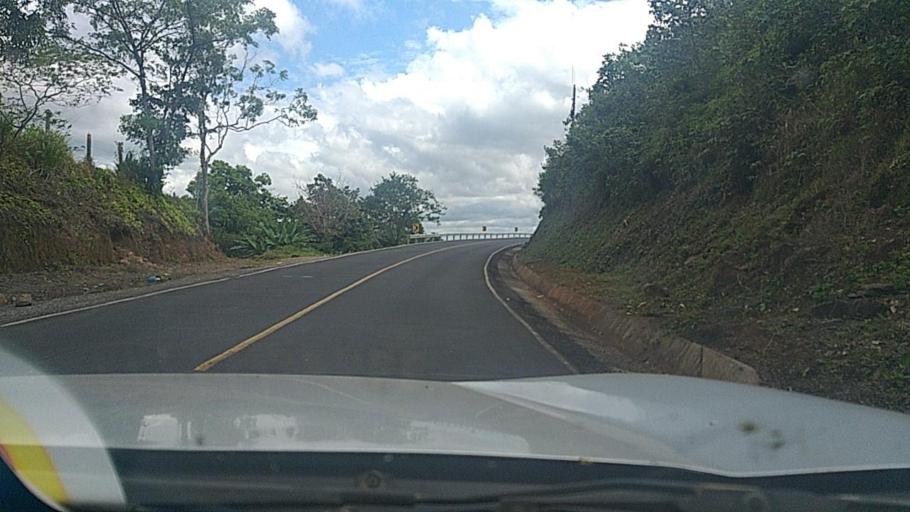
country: NI
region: Atlantico Sur
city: Muelle de los Bueyes
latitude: 12.1290
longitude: -84.4363
